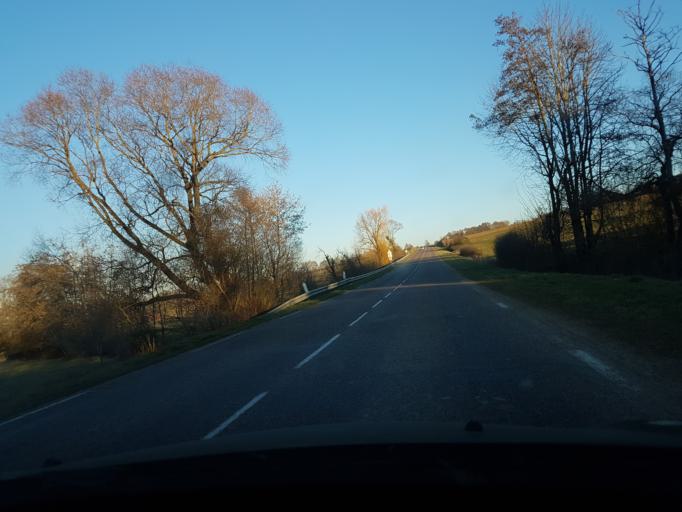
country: FR
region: Lorraine
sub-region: Departement des Vosges
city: Darney
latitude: 47.9330
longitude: 6.0706
